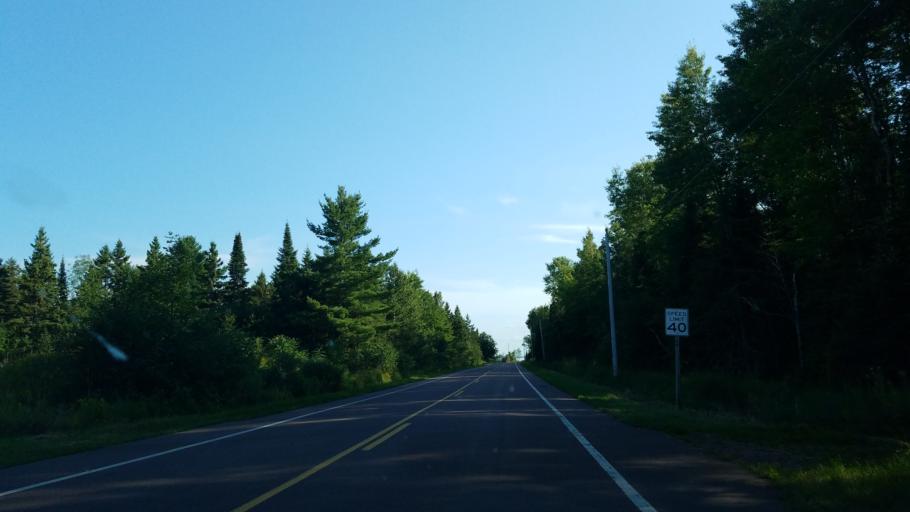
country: US
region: Wisconsin
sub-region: Bayfield County
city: Washburn
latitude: 46.7873
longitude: -90.7214
